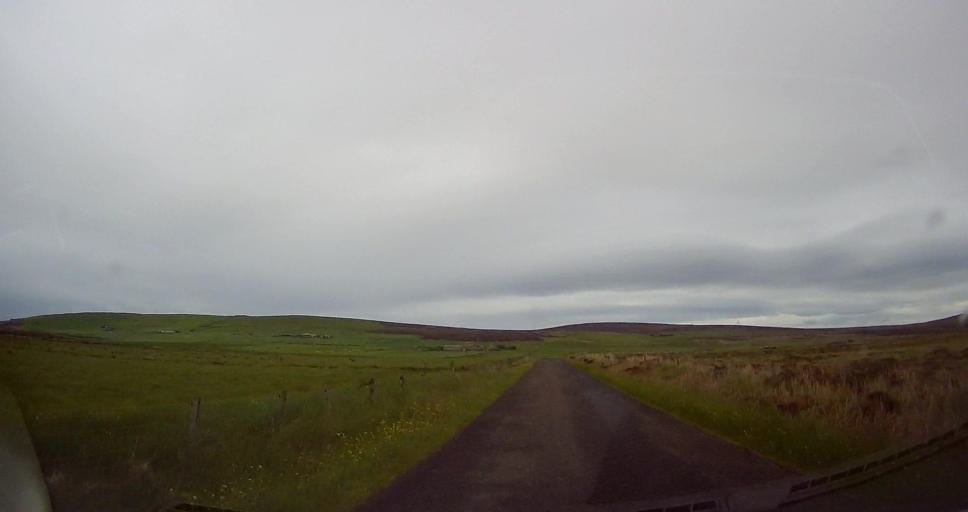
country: GB
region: Scotland
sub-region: Orkney Islands
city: Stromness
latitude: 59.0824
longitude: -3.1917
